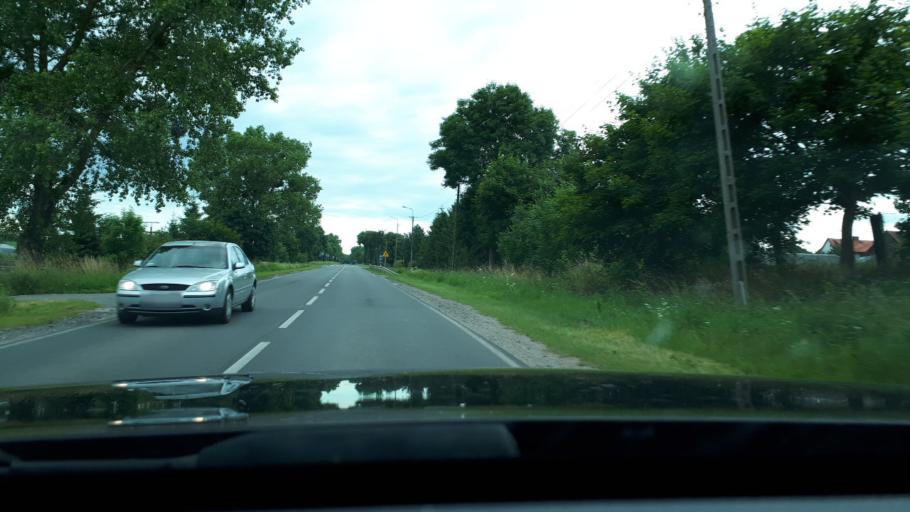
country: PL
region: Warmian-Masurian Voivodeship
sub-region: Powiat olsztynski
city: Olsztynek
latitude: 53.5759
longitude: 20.2760
